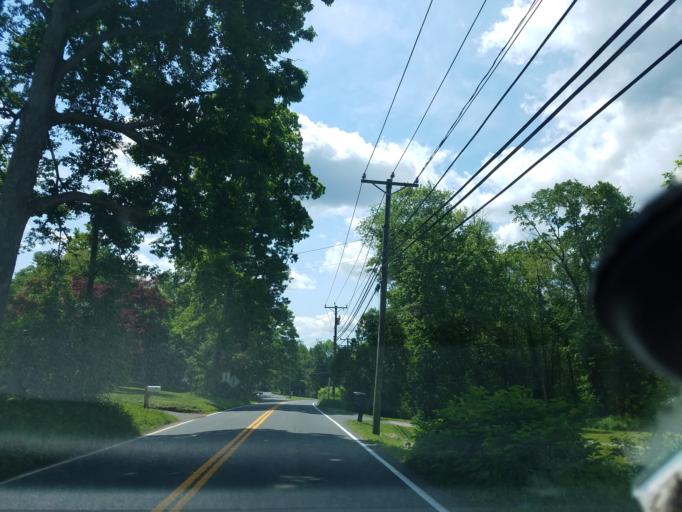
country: US
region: Connecticut
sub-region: Fairfield County
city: Sherman
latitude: 41.5044
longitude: -73.4692
